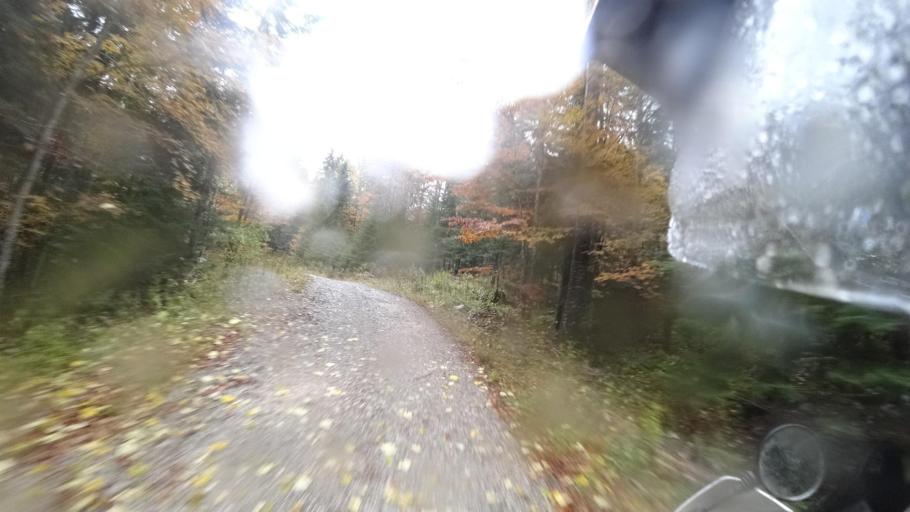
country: HR
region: Primorsko-Goranska
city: Vrbovsko
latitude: 45.3023
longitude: 14.9807
